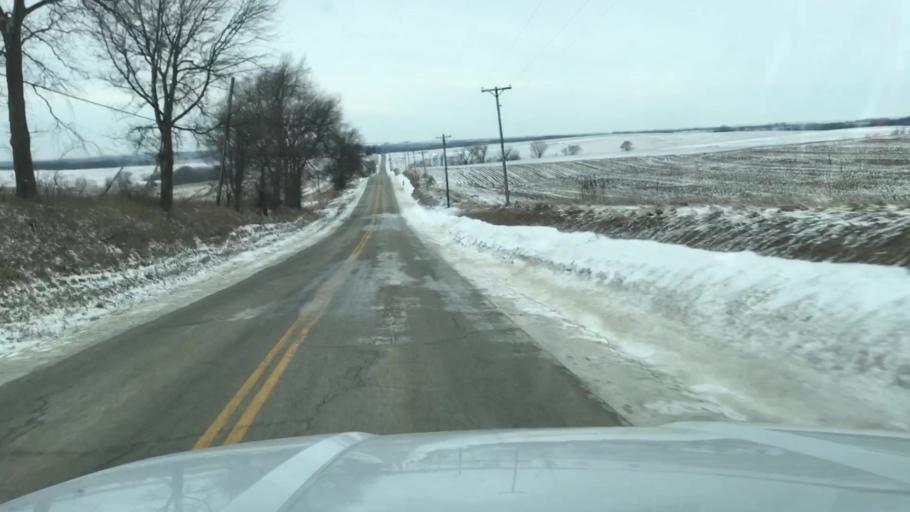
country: US
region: Missouri
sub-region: Andrew County
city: Savannah
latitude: 40.0249
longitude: -94.9414
